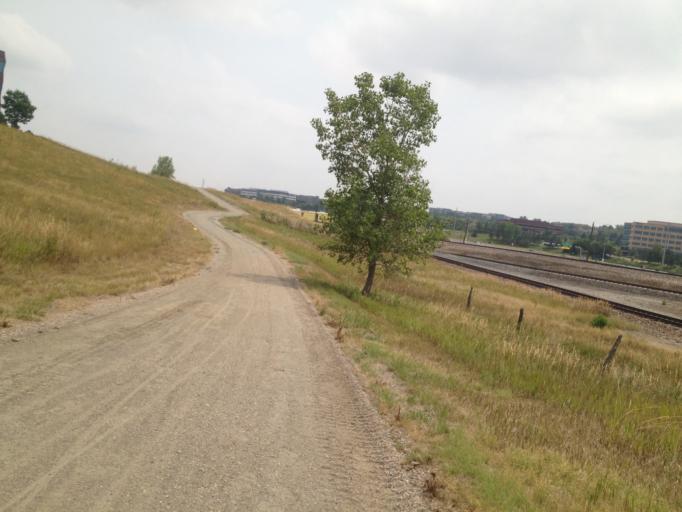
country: US
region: Colorado
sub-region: Broomfield County
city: Broomfield
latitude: 39.9283
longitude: -105.1119
